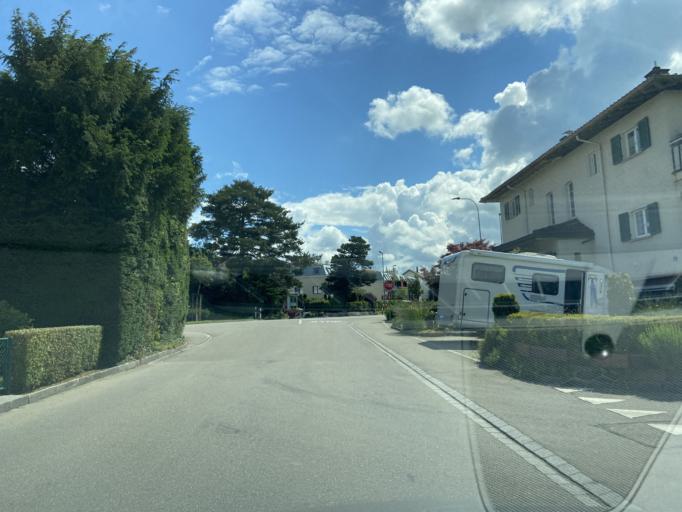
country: CH
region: Zurich
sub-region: Bezirk Winterthur
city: Wiesendangen / Wiesendangen (Dorf)
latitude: 47.5228
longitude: 8.7825
